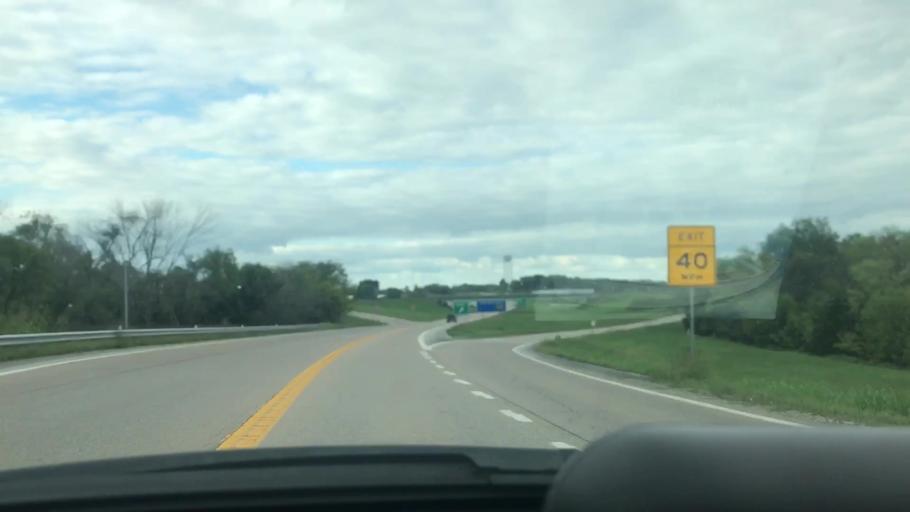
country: US
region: Missouri
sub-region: Benton County
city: Warsaw
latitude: 38.2390
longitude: -93.3603
